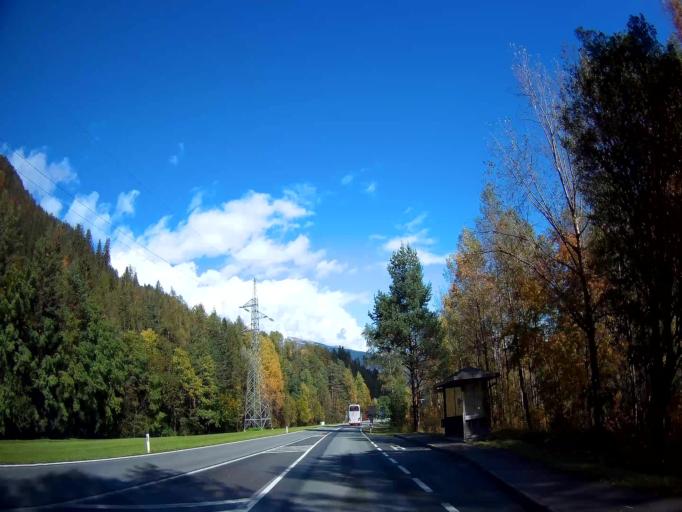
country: AT
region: Tyrol
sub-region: Politischer Bezirk Lienz
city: Leisach
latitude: 46.7973
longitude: 12.7347
